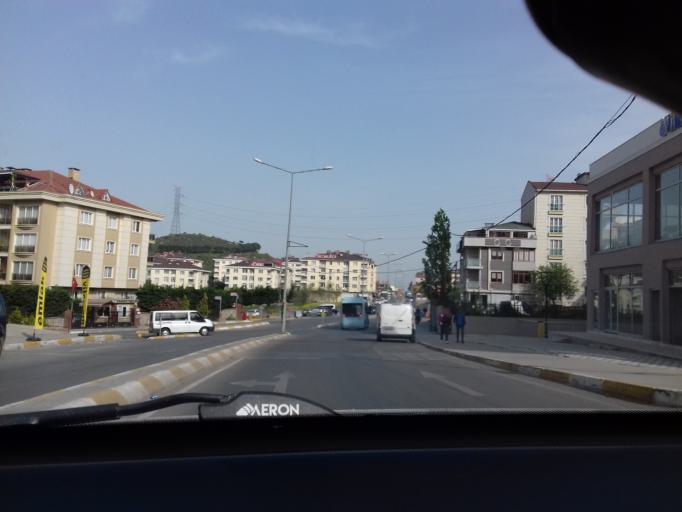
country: TR
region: Istanbul
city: Pendik
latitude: 40.9077
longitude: 29.2592
